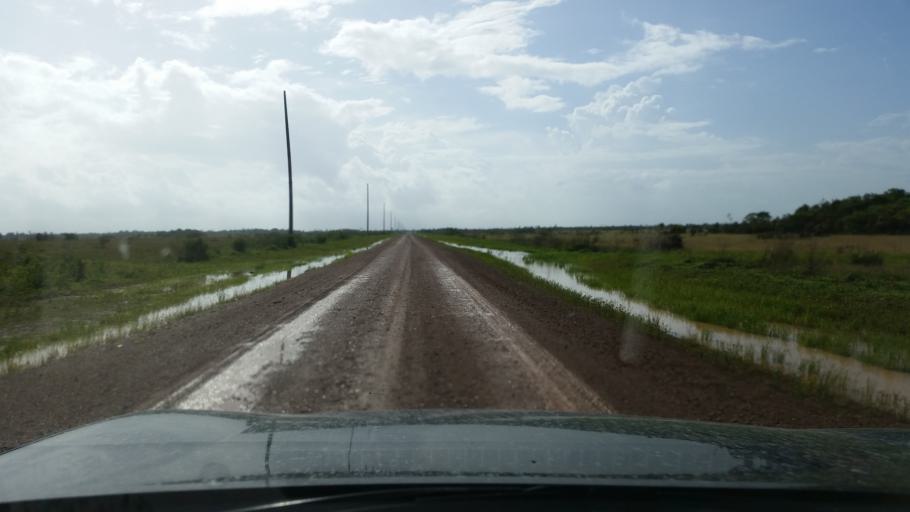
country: NI
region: Atlantico Norte (RAAN)
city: Puerto Cabezas
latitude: 14.1096
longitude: -83.5951
